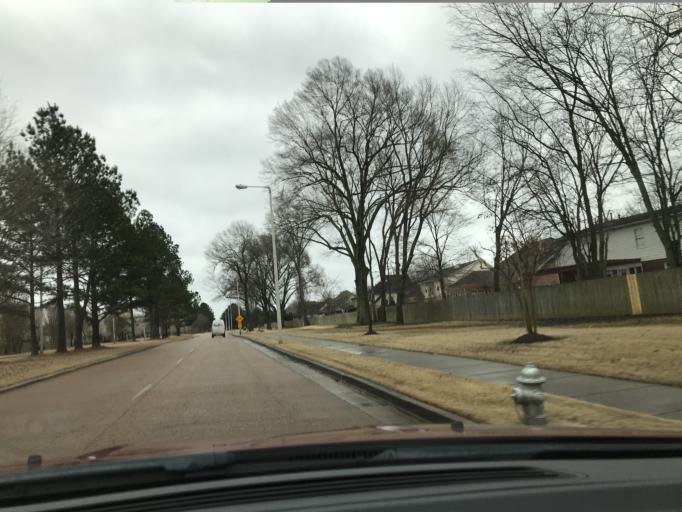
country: US
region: Tennessee
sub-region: Shelby County
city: Collierville
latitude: 35.0855
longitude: -89.6981
